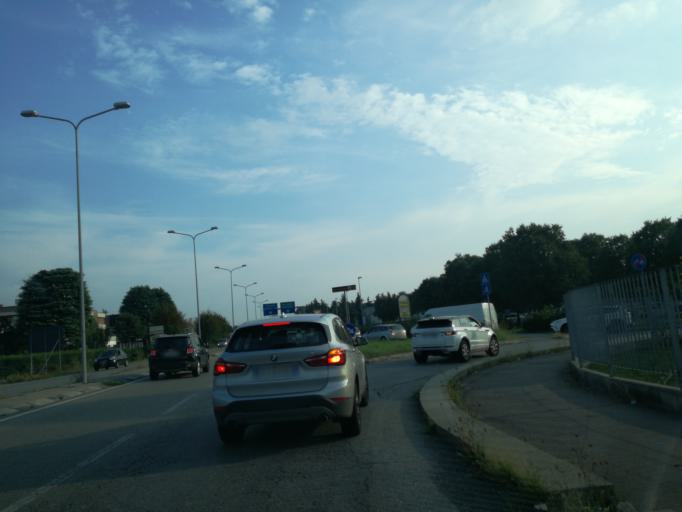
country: IT
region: Lombardy
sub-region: Citta metropolitana di Milano
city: Carugate
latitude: 45.5517
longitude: 9.3333
